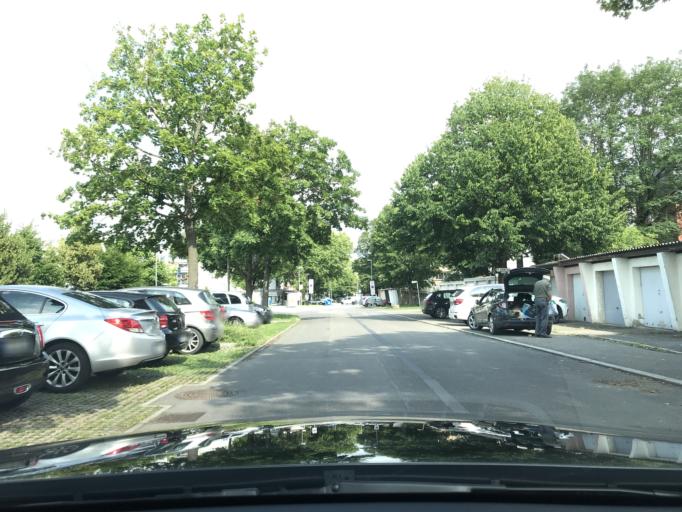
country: DE
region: Baden-Wuerttemberg
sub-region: Regierungsbezirk Stuttgart
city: Waiblingen
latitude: 48.8194
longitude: 9.3041
